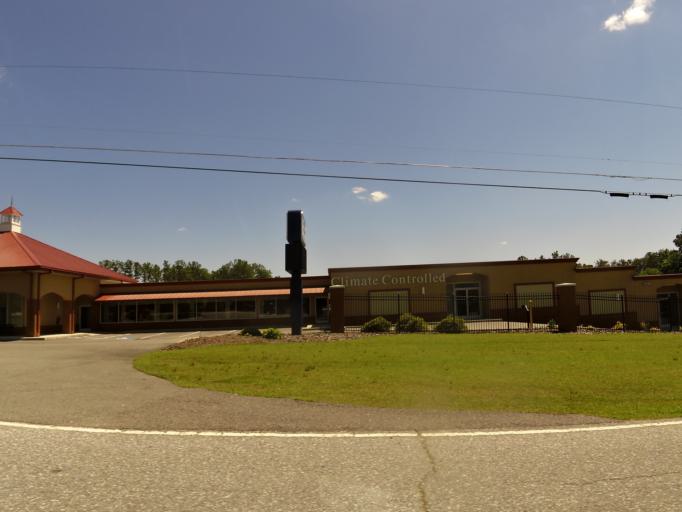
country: US
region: South Carolina
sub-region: Aiken County
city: Warrenville
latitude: 33.5625
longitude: -81.7734
